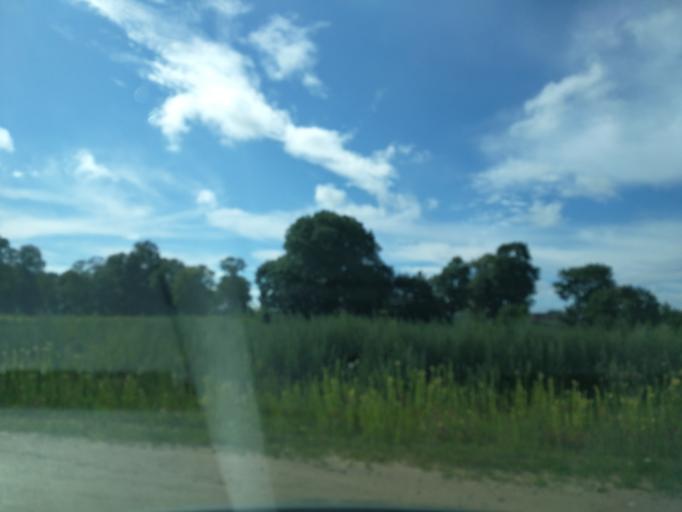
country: LV
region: Adazi
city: Adazi
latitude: 57.0948
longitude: 24.3181
